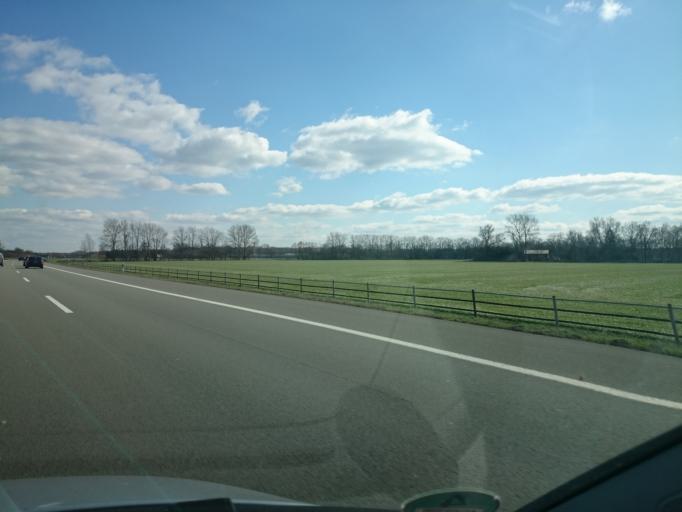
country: DE
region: Mecklenburg-Vorpommern
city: Neustadt-Glewe
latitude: 53.4115
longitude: 11.5605
